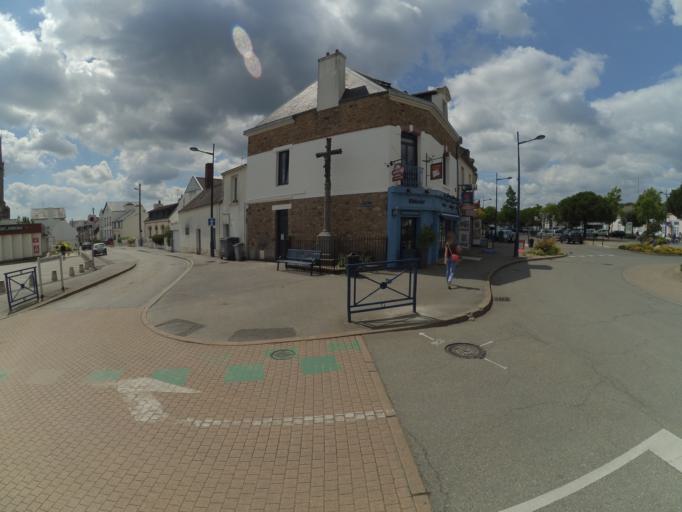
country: FR
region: Brittany
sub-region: Departement du Morbihan
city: Auray
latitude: 47.6796
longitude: -2.9991
